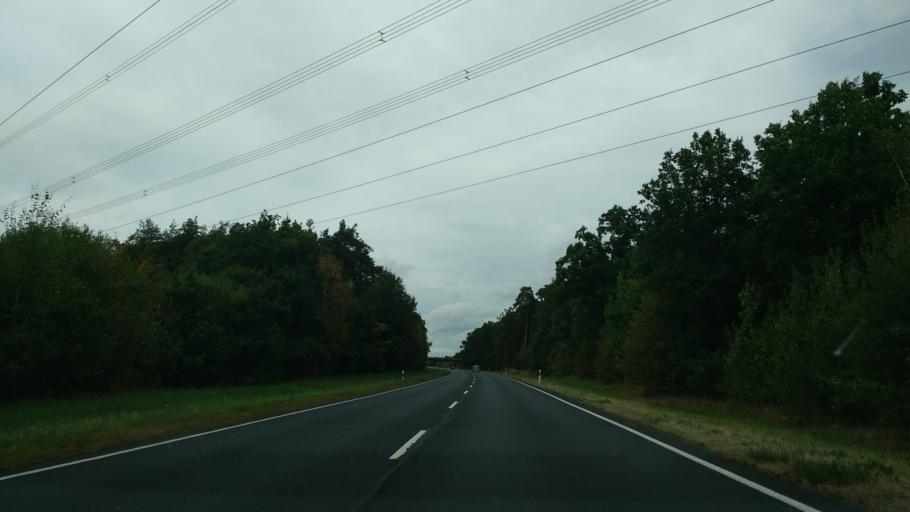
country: DE
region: Bavaria
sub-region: Regierungsbezirk Unterfranken
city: Schwebheim
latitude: 49.9706
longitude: 10.2602
